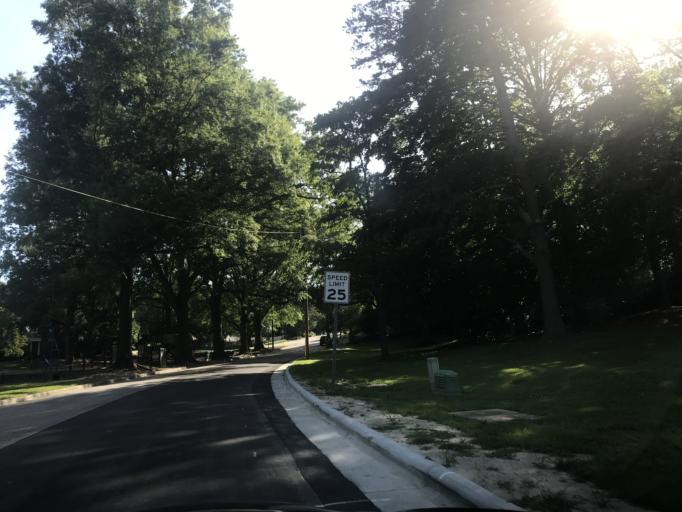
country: US
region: North Carolina
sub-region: Wake County
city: West Raleigh
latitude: 35.7951
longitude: -78.6797
